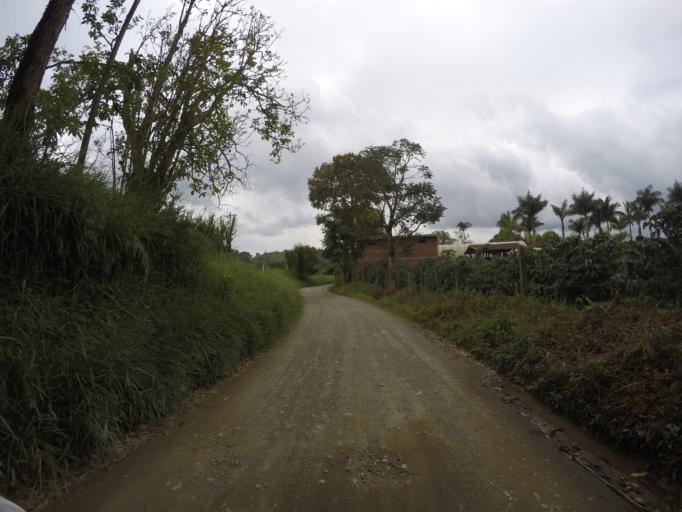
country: CO
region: Quindio
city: Filandia
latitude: 4.6429
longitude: -75.6776
